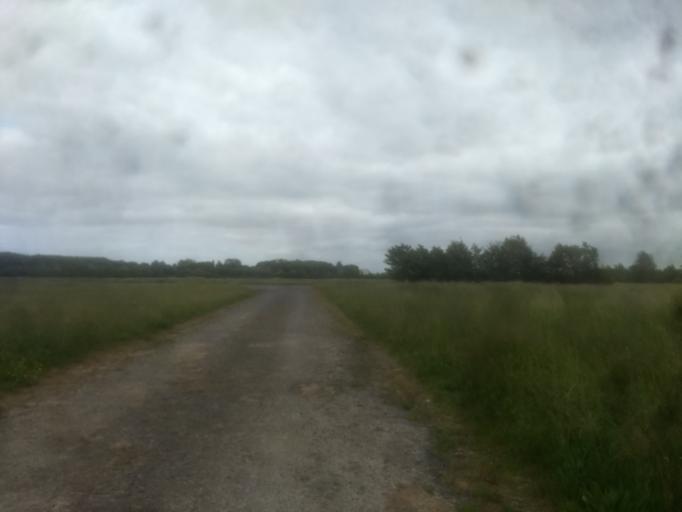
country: FR
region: Nord-Pas-de-Calais
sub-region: Departement du Pas-de-Calais
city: Tilloy-les-Mofflaines
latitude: 50.2750
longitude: 2.8055
